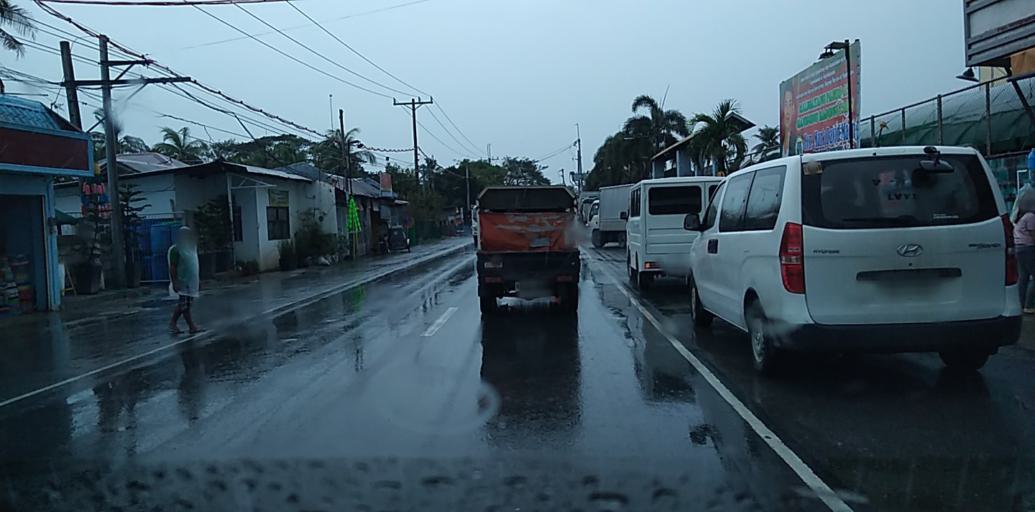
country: PH
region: Central Luzon
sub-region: Province of Bulacan
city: Bulualto
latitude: 15.2084
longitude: 120.9561
